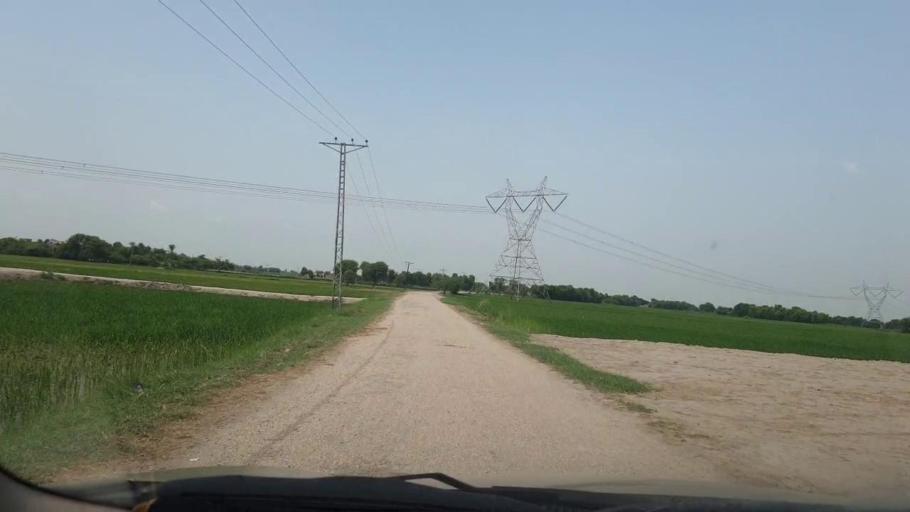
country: PK
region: Sindh
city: Larkana
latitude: 27.5796
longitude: 68.1431
